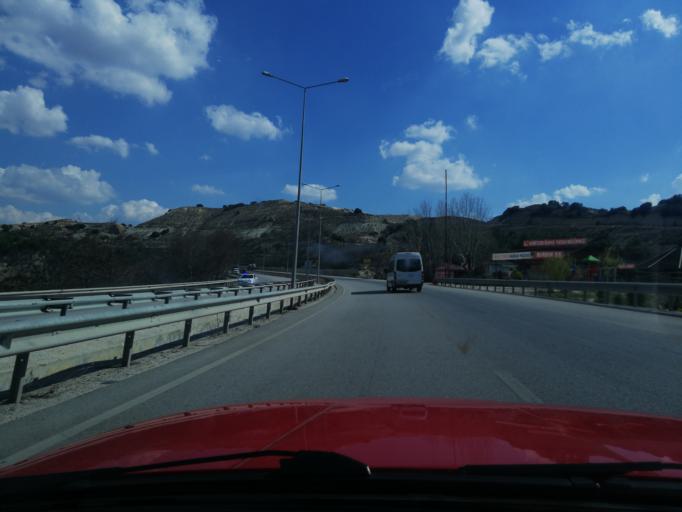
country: TR
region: Burdur
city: Burdur
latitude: 37.7030
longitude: 30.3071
